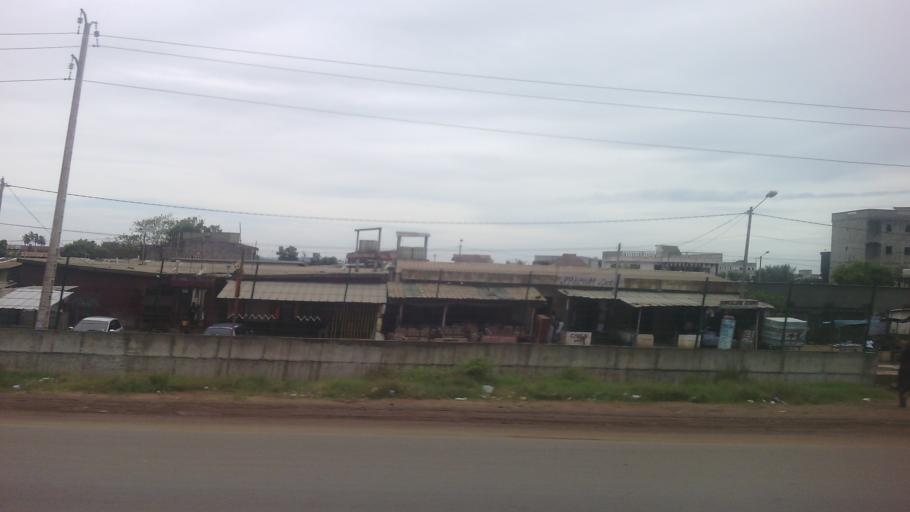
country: CI
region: Lagunes
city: Bingerville
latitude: 5.2391
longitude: -3.8945
